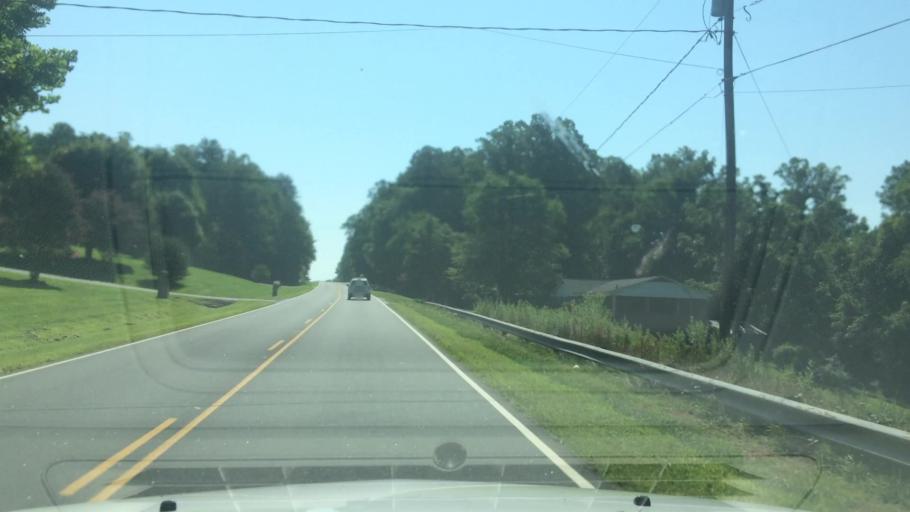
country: US
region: North Carolina
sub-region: Caldwell County
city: Hudson
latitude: 35.9091
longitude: -81.4237
